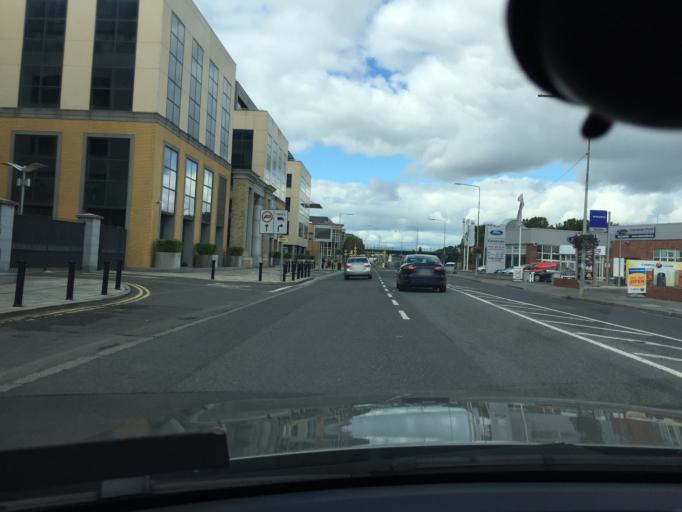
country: IE
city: Fairview
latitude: 53.3571
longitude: -6.2329
